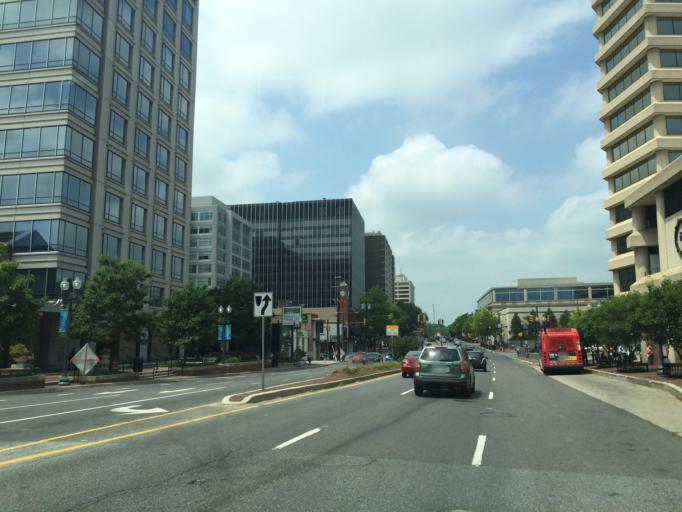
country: US
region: Maryland
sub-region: Montgomery County
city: Friendship Village
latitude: 38.9610
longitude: -77.0857
